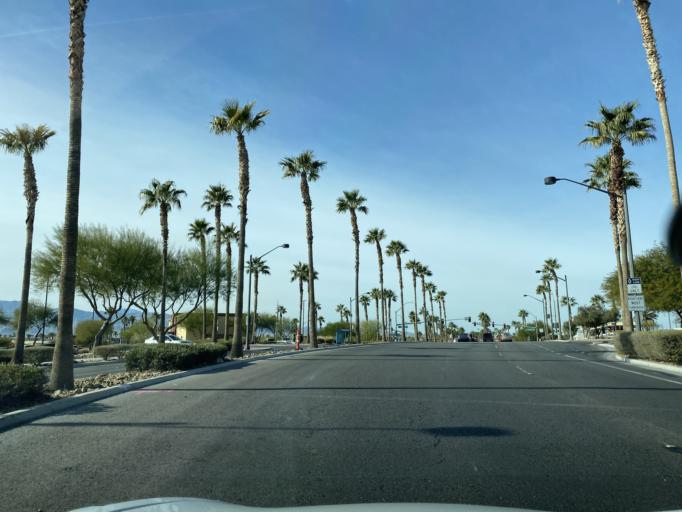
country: US
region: Nevada
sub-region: Clark County
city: Las Vegas
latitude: 36.2708
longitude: -115.2632
